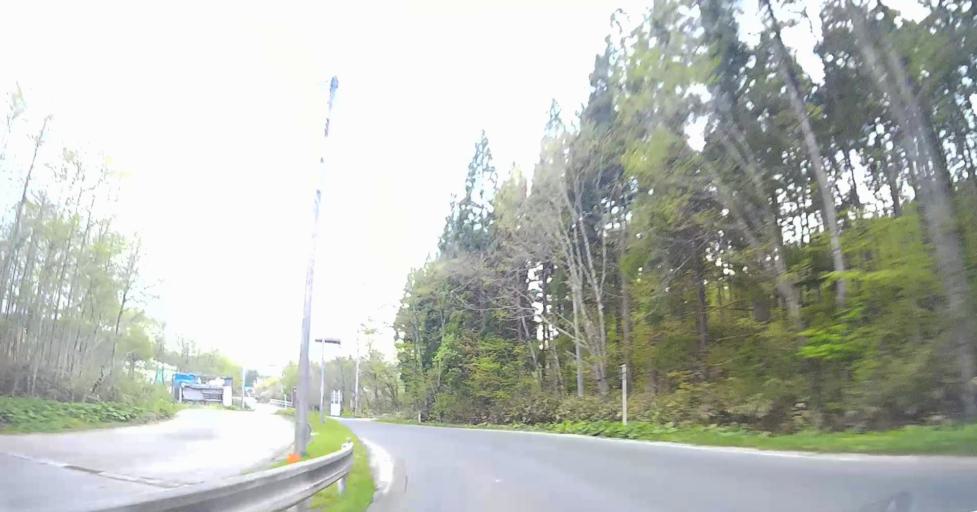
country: JP
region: Aomori
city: Goshogawara
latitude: 41.0906
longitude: 140.5528
